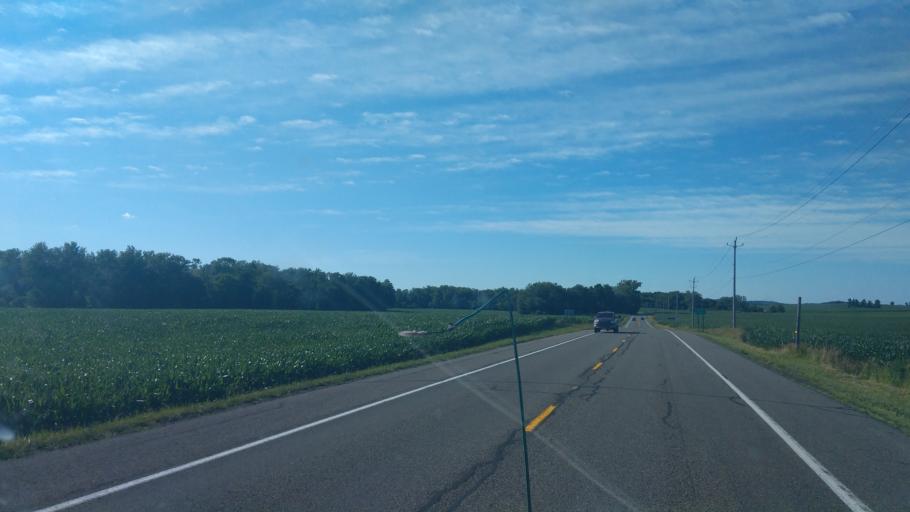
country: US
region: New York
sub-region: Wayne County
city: Lyons
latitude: 43.0132
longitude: -76.9842
